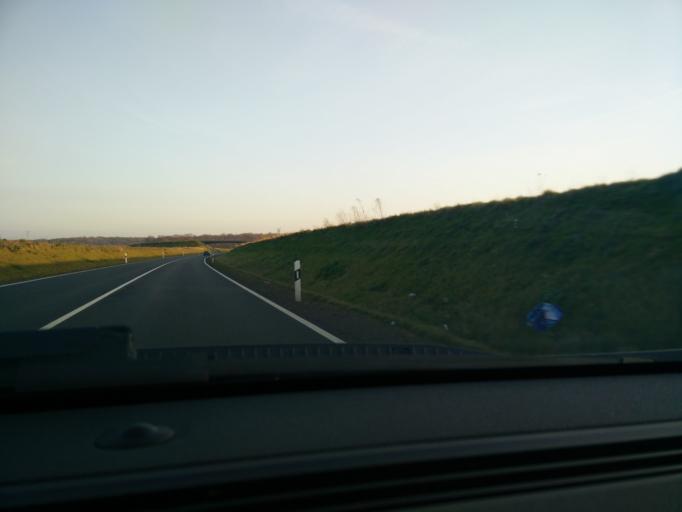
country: DE
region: Saxony
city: Grossposna
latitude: 51.2499
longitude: 12.4796
